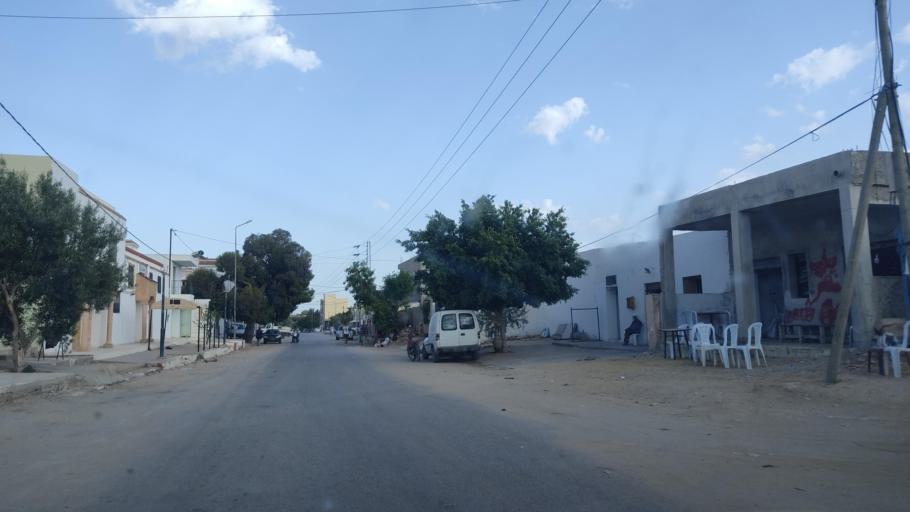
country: TN
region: Safaqis
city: Sfax
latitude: 34.8459
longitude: 10.6163
